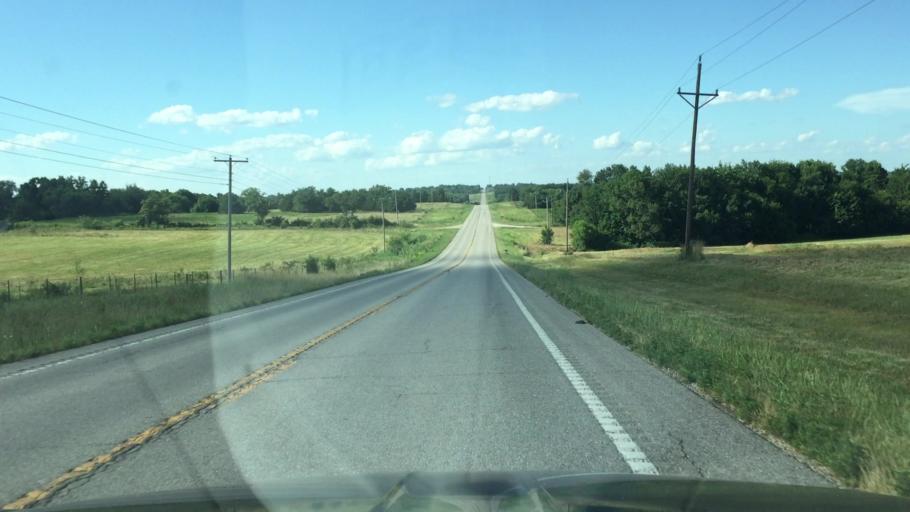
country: US
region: Missouri
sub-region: Morgan County
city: Versailles
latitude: 38.5385
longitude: -92.7980
